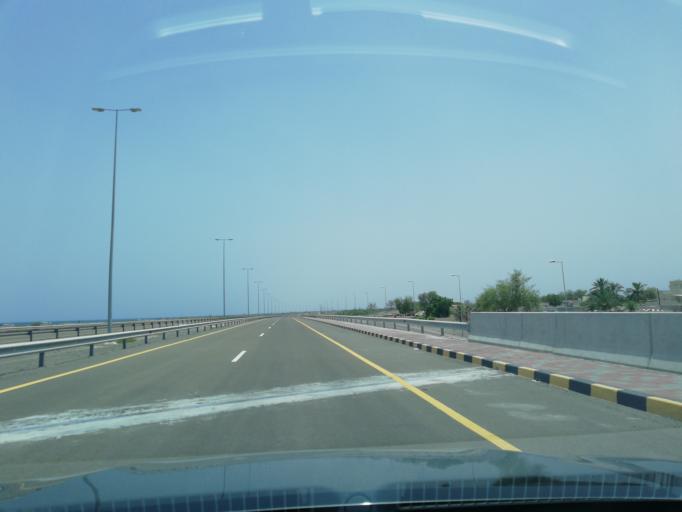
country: OM
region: Al Batinah
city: Shinas
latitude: 24.8965
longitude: 56.3983
